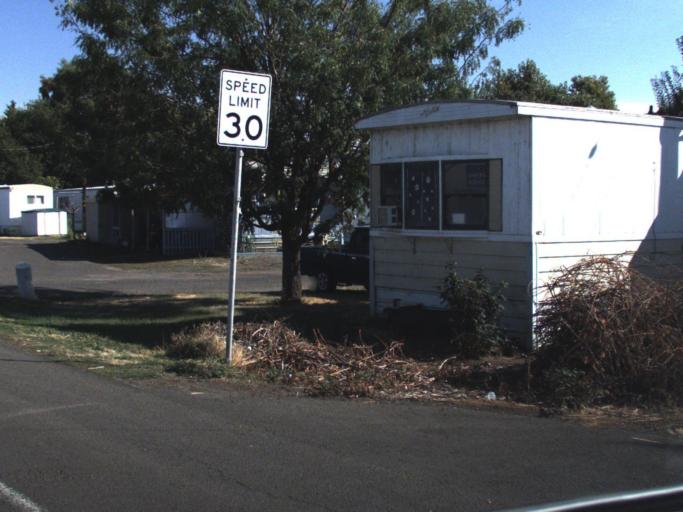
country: US
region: Washington
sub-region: Walla Walla County
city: College Place
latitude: 46.0052
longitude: -118.3891
